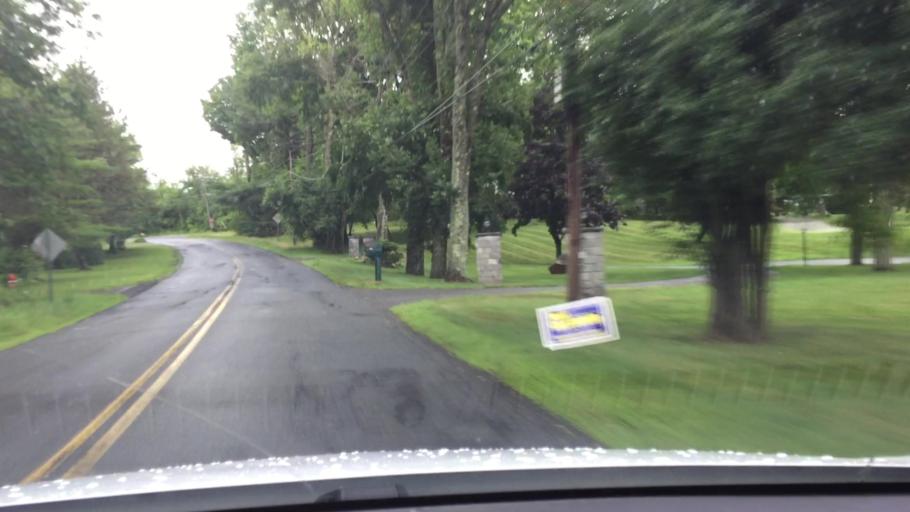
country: US
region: Massachusetts
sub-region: Berkshire County
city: Dalton
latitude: 42.4272
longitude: -73.1941
